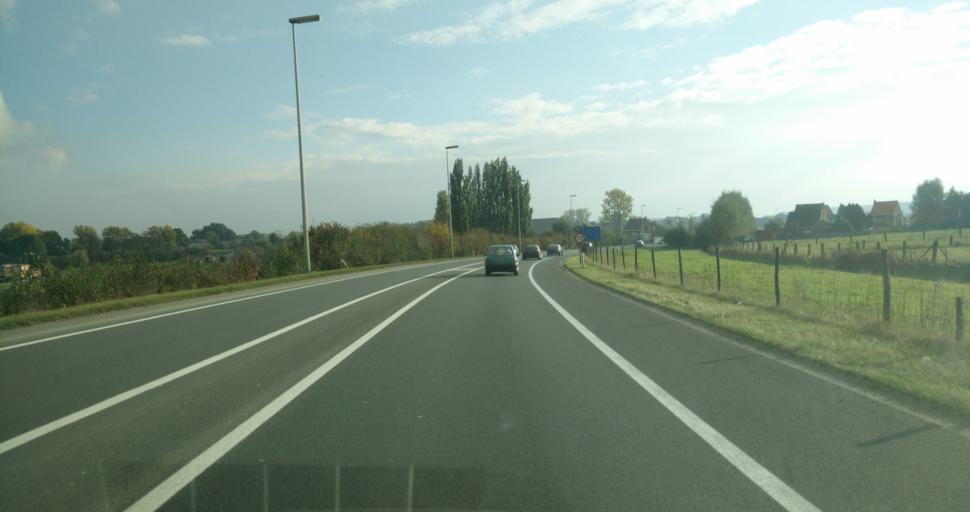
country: BE
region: Flanders
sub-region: Provincie Oost-Vlaanderen
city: Oosterzele
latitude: 50.9457
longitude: 3.8223
